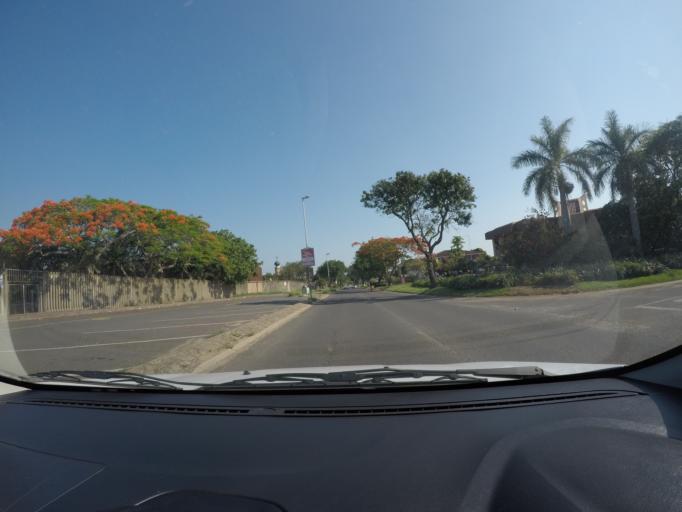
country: ZA
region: KwaZulu-Natal
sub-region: uThungulu District Municipality
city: Richards Bay
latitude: -28.7234
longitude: 32.0414
